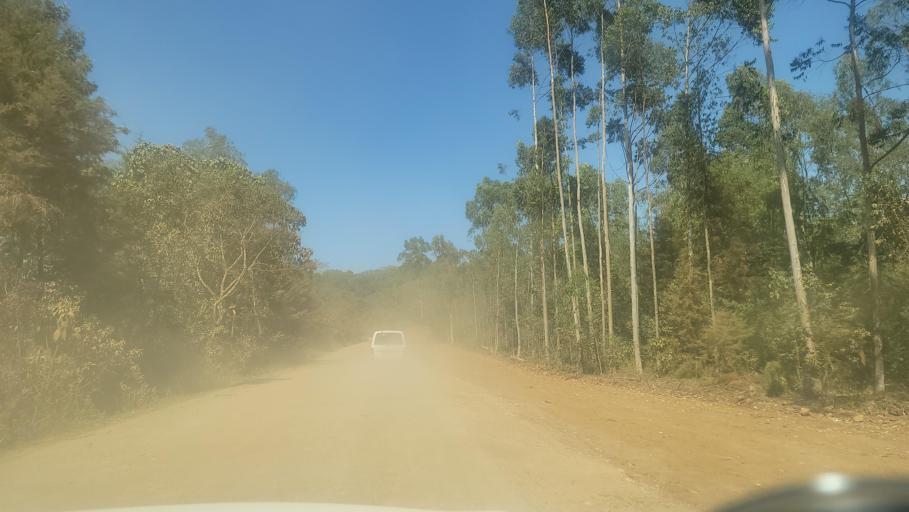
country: ET
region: Oromiya
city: Agaro
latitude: 7.7860
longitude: 36.4066
